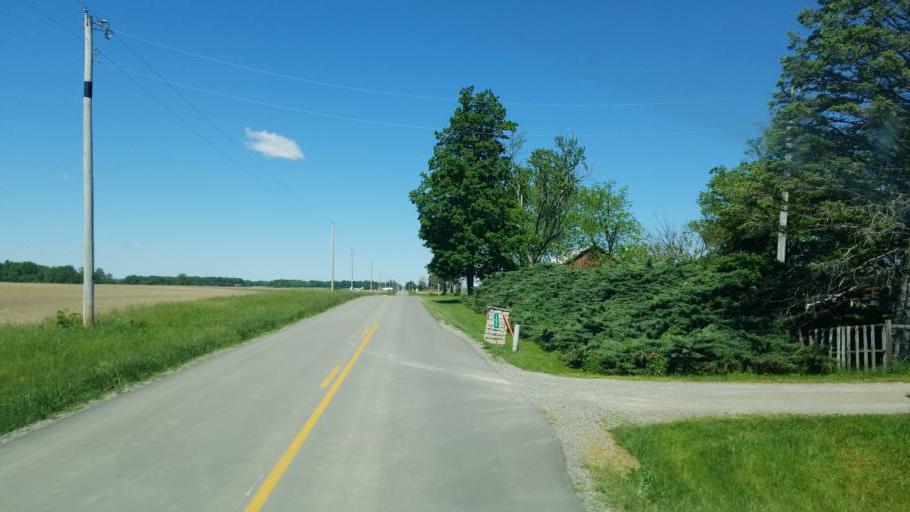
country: US
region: Ohio
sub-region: Shelby County
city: Jackson Center
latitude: 40.4174
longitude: -83.9703
